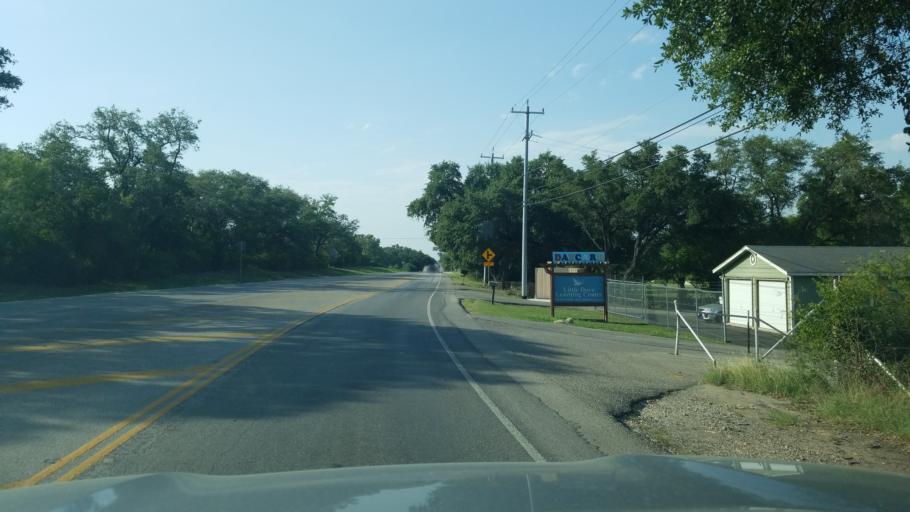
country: US
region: Texas
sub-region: Bexar County
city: Helotes
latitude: 29.4608
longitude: -98.7580
